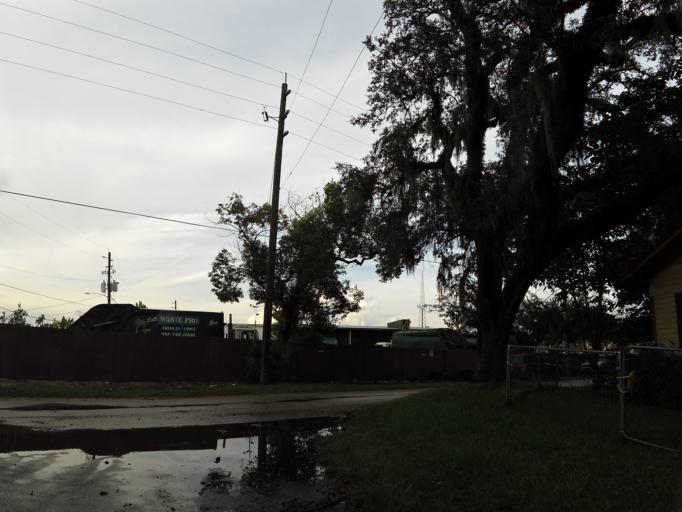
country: US
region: Florida
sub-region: Duval County
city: Jacksonville
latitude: 30.3284
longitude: -81.7037
